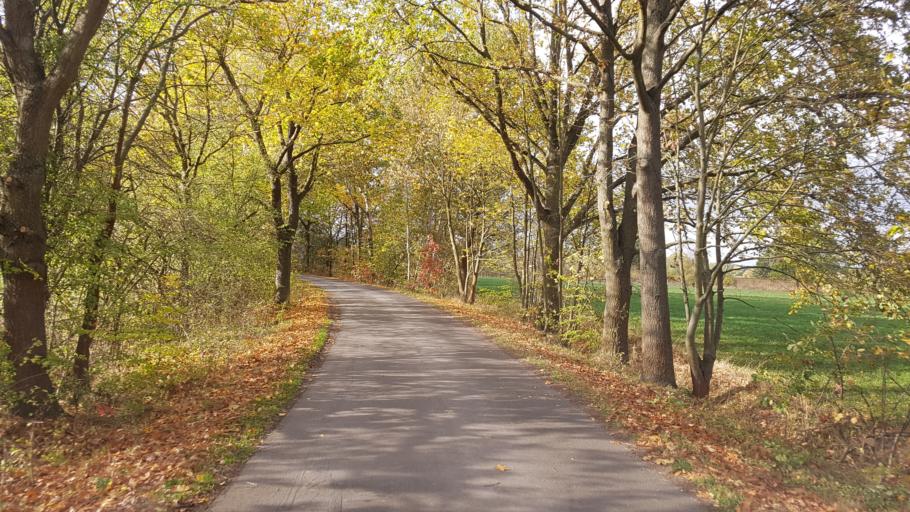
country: DE
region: Brandenburg
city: Schonborn
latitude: 51.6109
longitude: 13.5248
